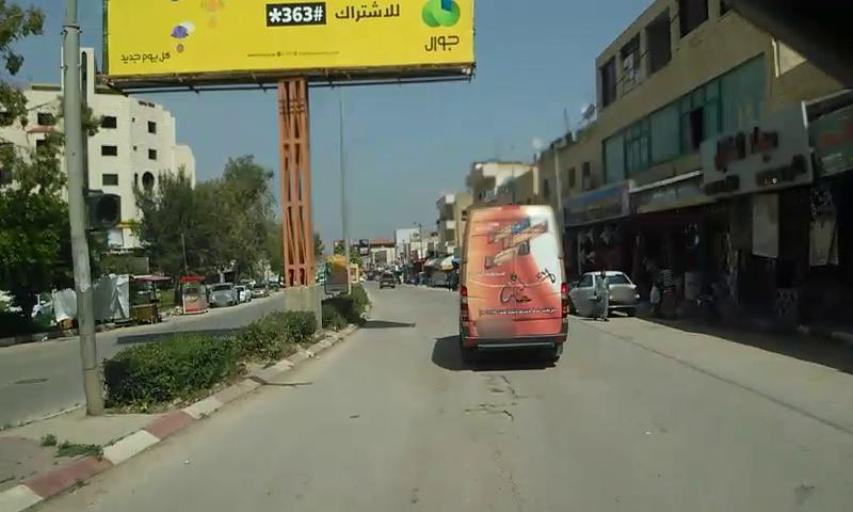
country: PS
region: West Bank
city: Janin
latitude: 32.4646
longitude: 35.3047
